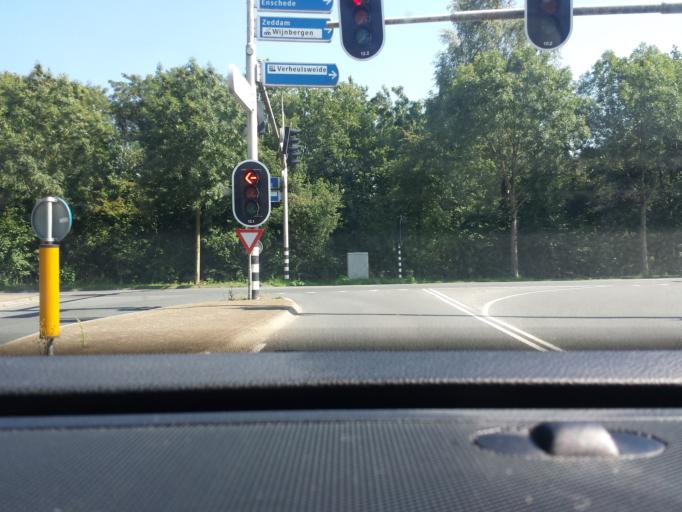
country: NL
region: Gelderland
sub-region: Gemeente Doetinchem
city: Doetinchem
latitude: 51.9605
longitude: 6.2768
